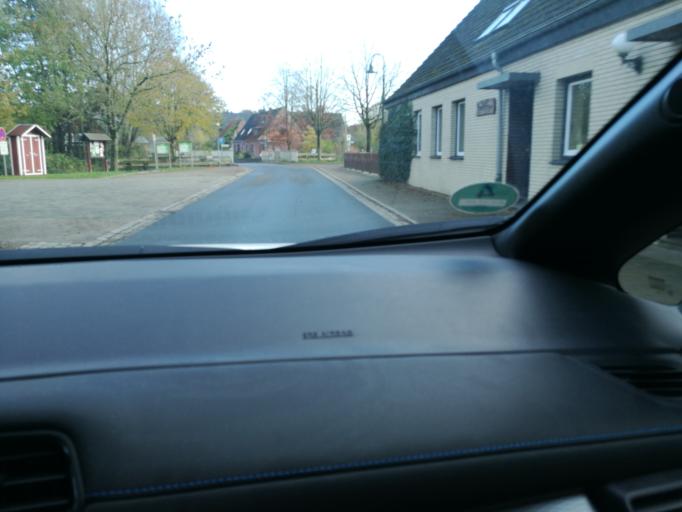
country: DE
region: Schleswig-Holstein
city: Bunsdorf
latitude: 54.3701
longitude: 9.7438
